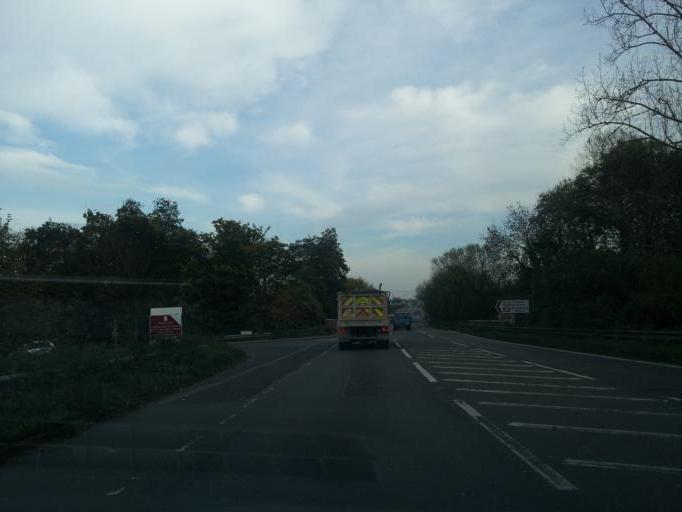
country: GB
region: England
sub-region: Cambridgeshire
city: Duxford
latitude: 52.1035
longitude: 0.1684
